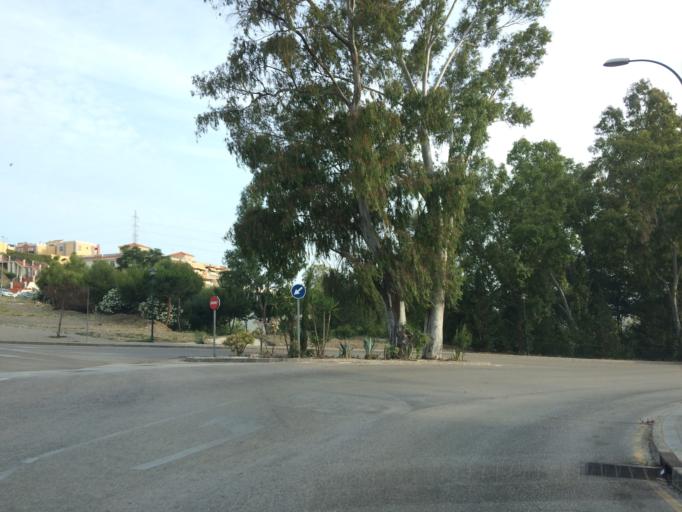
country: ES
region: Andalusia
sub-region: Provincia de Malaga
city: Malaga
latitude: 36.7373
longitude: -4.4117
